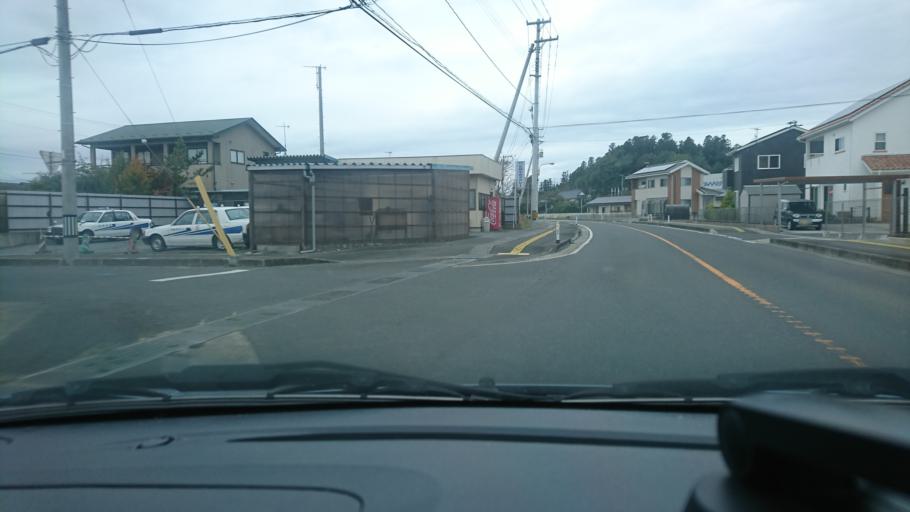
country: JP
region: Iwate
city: Ichinoseki
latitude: 38.7726
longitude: 141.1237
